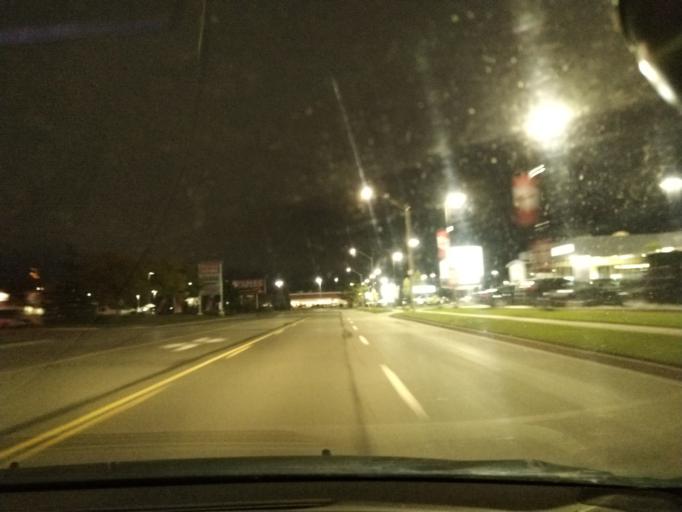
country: CA
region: Ontario
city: Innisfil
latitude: 44.3365
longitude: -79.6879
